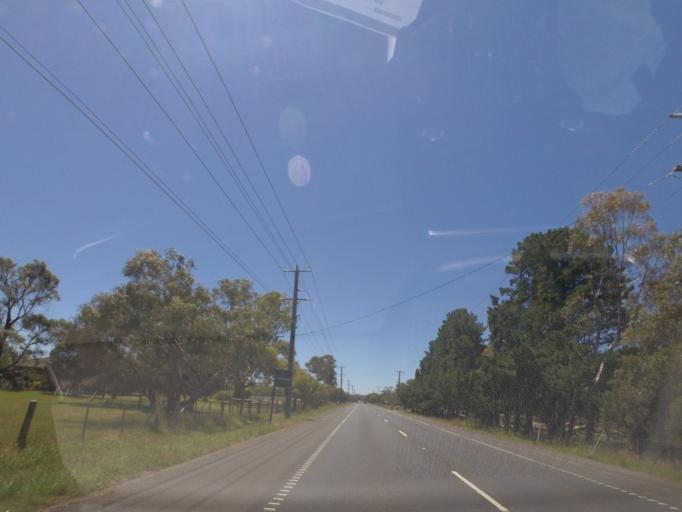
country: AU
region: Victoria
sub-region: Whittlesea
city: Mernda
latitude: -37.5556
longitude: 145.0313
